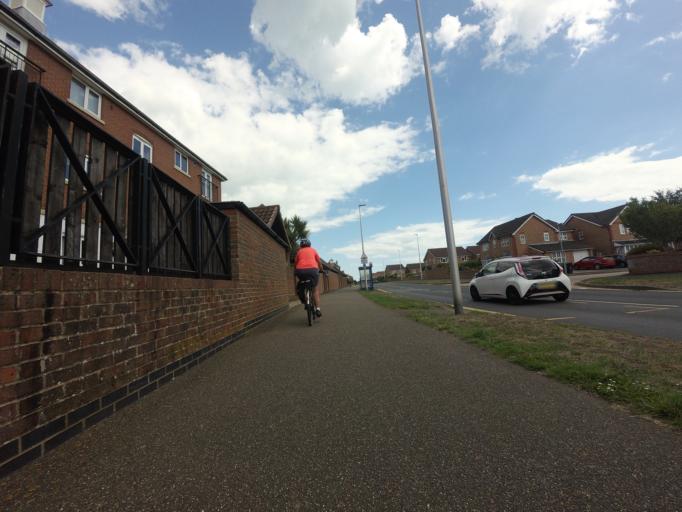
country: GB
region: England
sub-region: East Sussex
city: Pevensey
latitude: 50.7896
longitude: 0.3228
